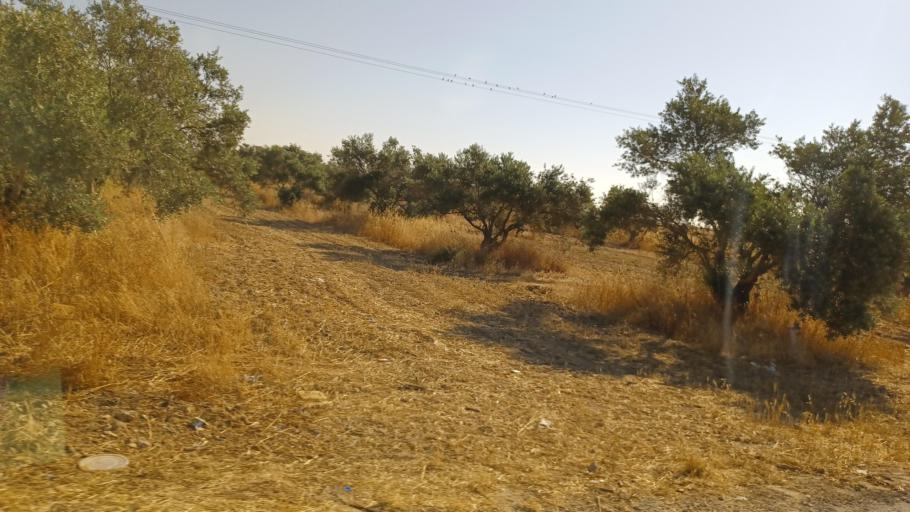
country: CY
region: Larnaka
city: Athienou
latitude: 35.0674
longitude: 33.5252
